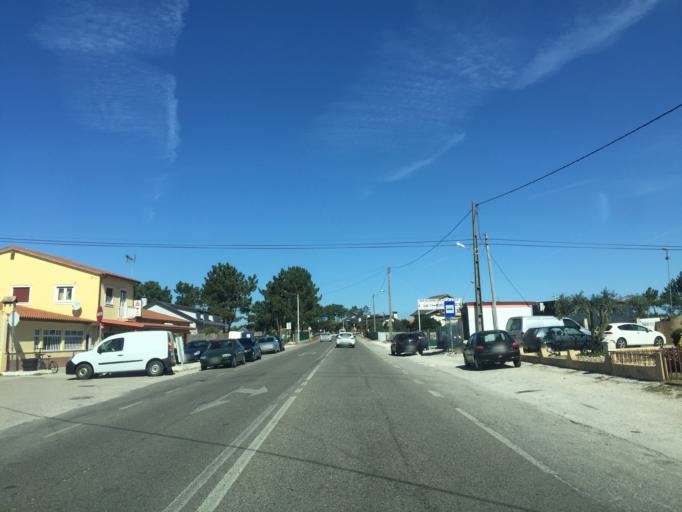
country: PT
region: Coimbra
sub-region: Figueira da Foz
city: Alhadas
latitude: 40.2556
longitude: -8.7809
